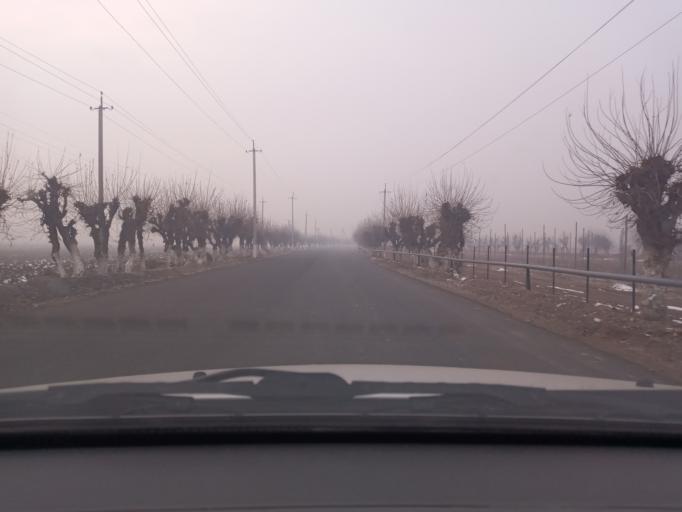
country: UZ
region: Namangan
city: Pop
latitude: 40.8717
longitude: 71.1469
